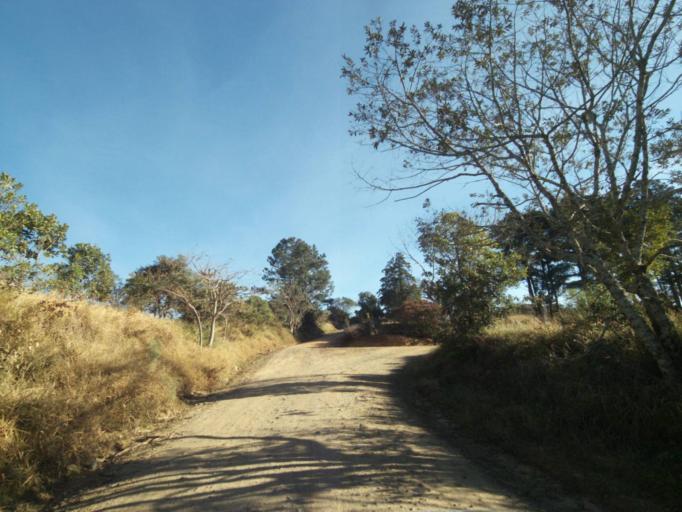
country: BR
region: Parana
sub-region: Tibagi
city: Tibagi
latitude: -24.5476
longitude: -50.6194
